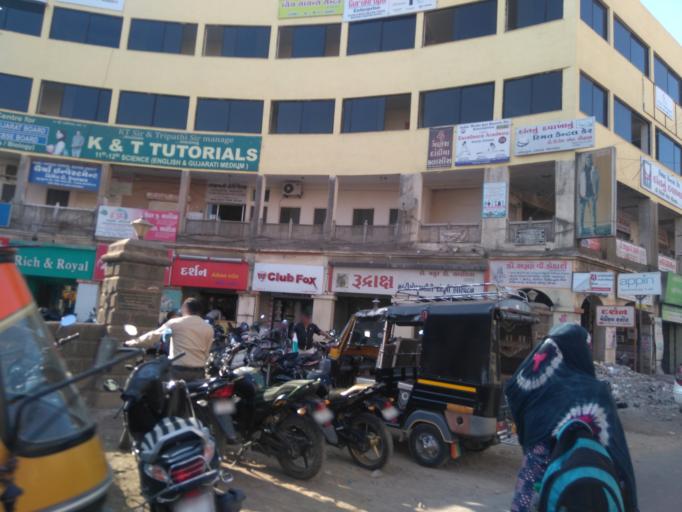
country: IN
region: Gujarat
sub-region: Junagadh
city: Junagadh
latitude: 21.5107
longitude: 70.4519
